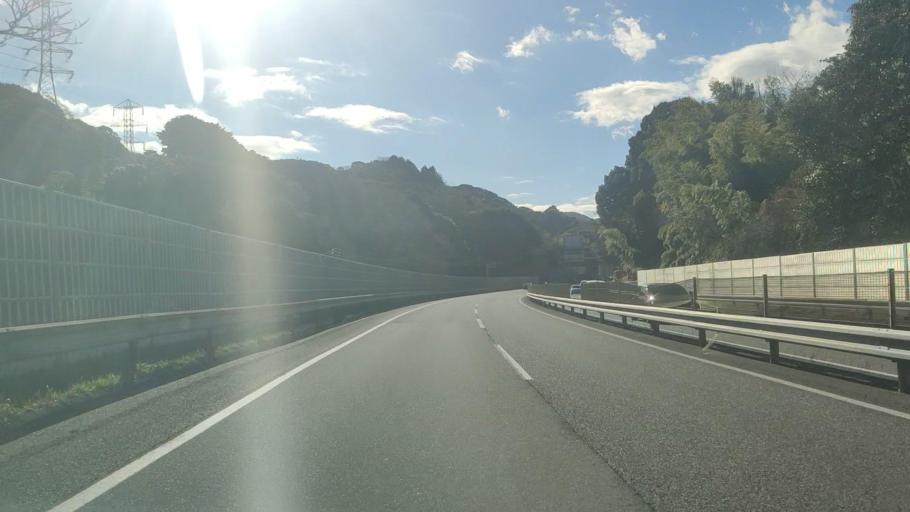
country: JP
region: Fukuoka
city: Kitakyushu
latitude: 33.8559
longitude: 130.8420
